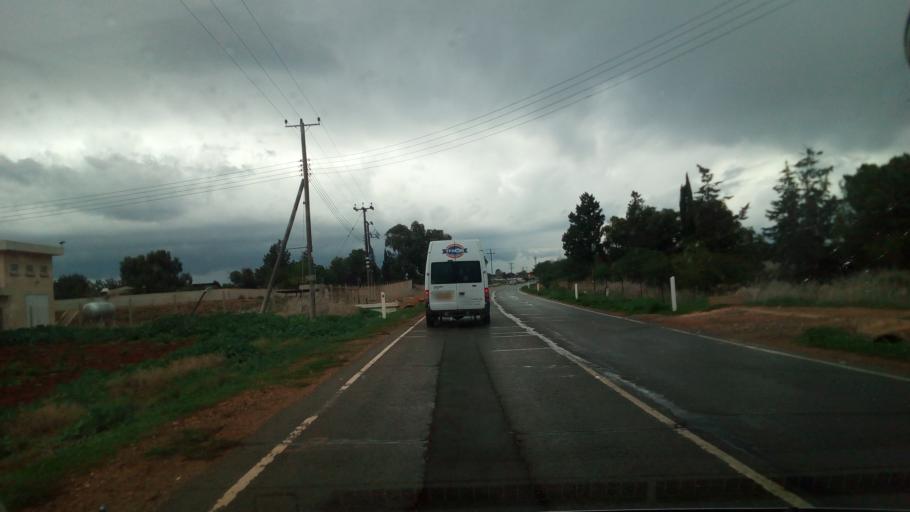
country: CY
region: Ammochostos
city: Liopetri
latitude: 34.9918
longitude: 33.8922
